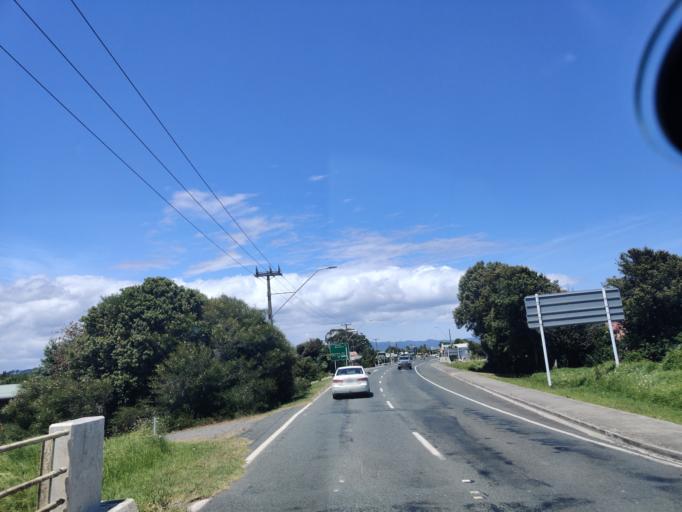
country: NZ
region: Northland
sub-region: Far North District
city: Kaitaia
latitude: -35.0444
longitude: 173.2567
